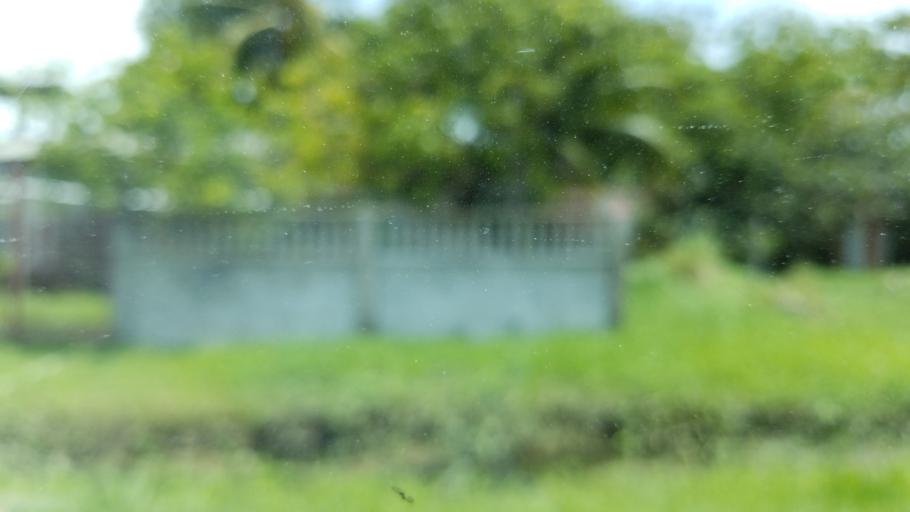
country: GY
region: Demerara-Mahaica
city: Georgetown
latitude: 6.7957
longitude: -58.1194
